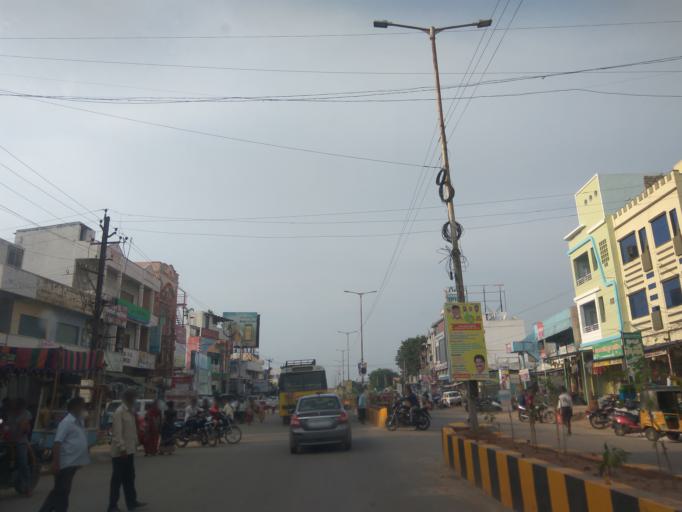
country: IN
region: Andhra Pradesh
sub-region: Guntur
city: Vinukonda
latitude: 16.0518
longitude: 79.7402
